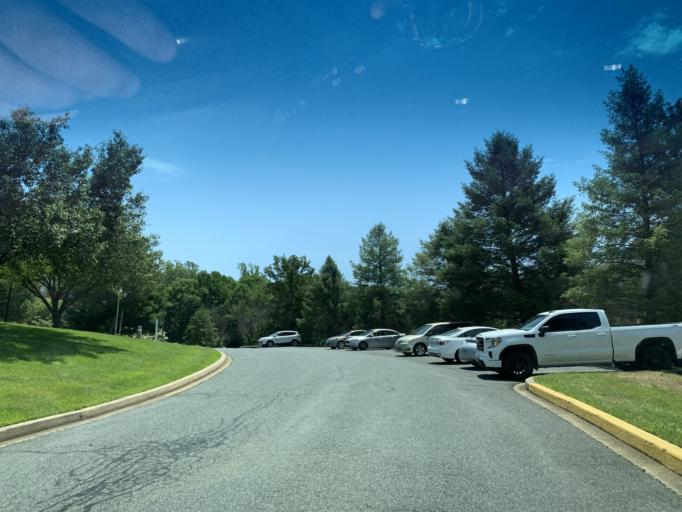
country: US
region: Maryland
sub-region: Harford County
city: Bel Air North
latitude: 39.5631
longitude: -76.3754
